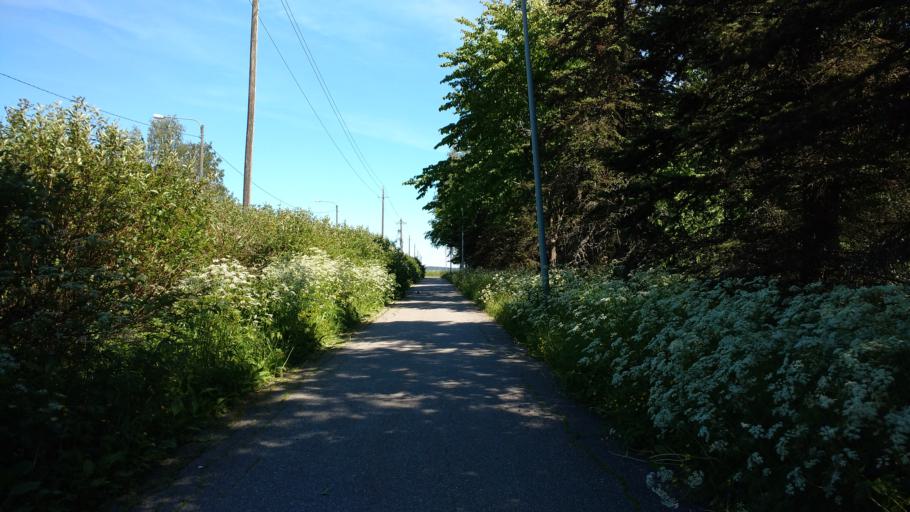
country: FI
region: Varsinais-Suomi
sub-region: Salo
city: Salo
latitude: 60.4018
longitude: 23.1462
